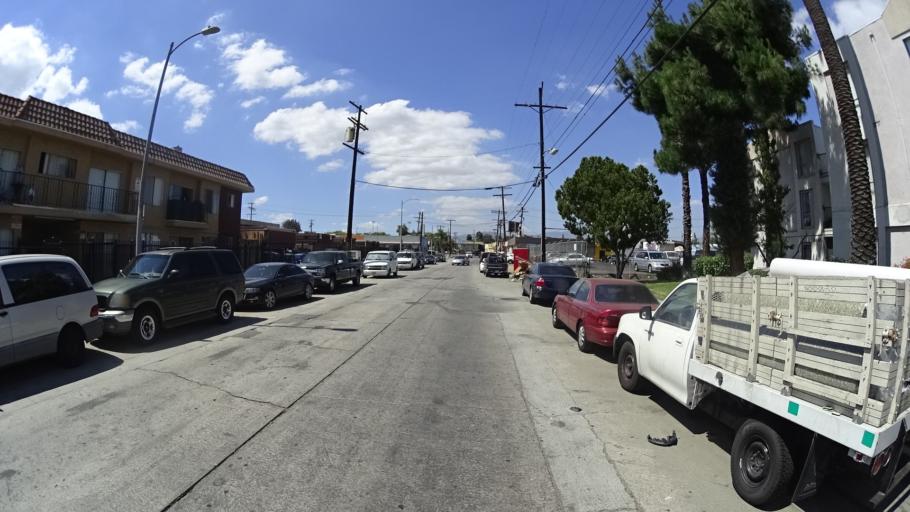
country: US
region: California
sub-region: Los Angeles County
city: Van Nuys
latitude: 34.2272
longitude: -118.4656
